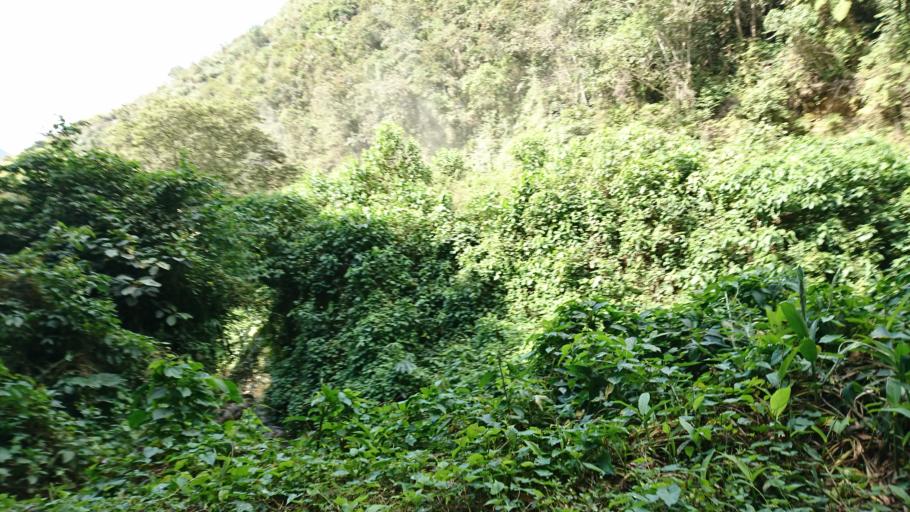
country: BO
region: La Paz
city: Coroico
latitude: -16.1284
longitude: -67.7658
